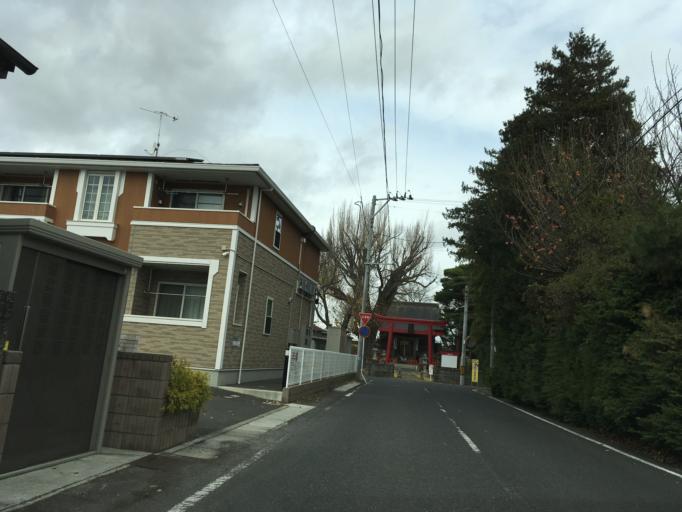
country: JP
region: Miyagi
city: Wakuya
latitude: 38.6918
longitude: 141.1985
